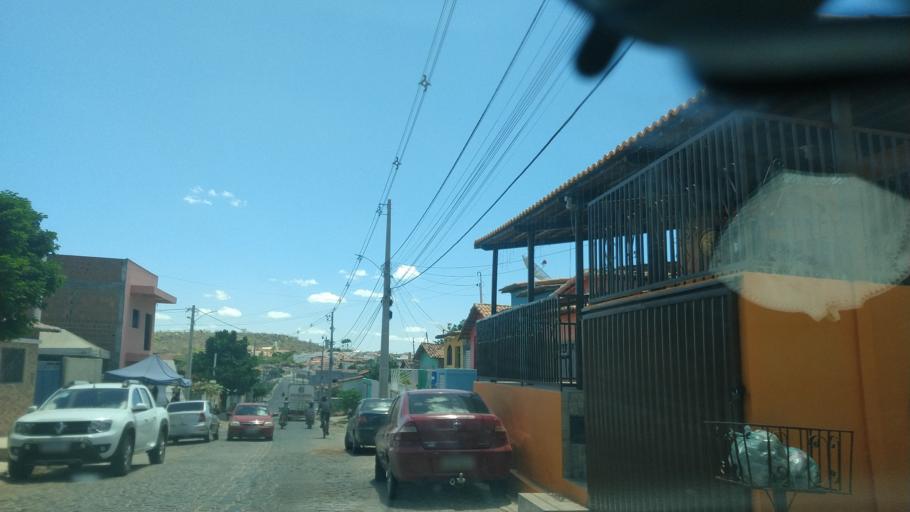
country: BR
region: Rio Grande do Norte
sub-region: Cerro Cora
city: Cerro Cora
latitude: -6.0381
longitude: -36.3470
